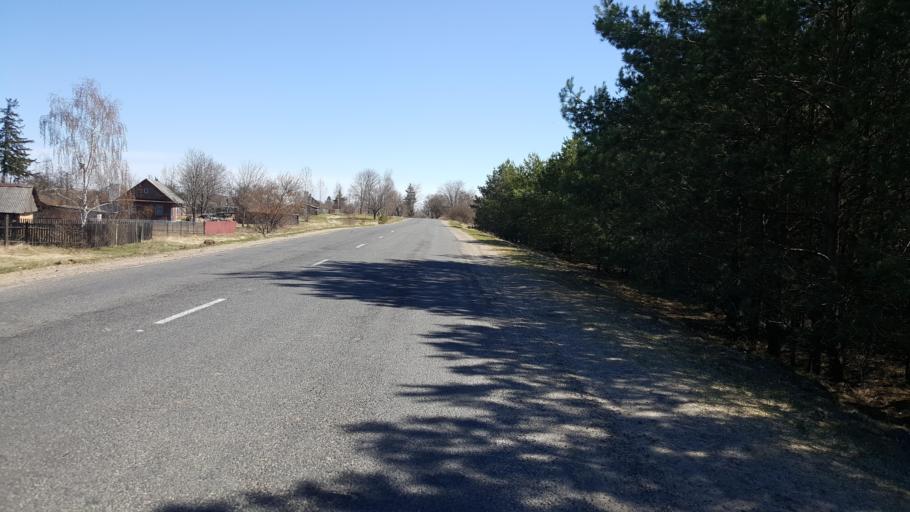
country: BY
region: Brest
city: Charnawchytsy
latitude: 52.2599
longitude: 23.8566
